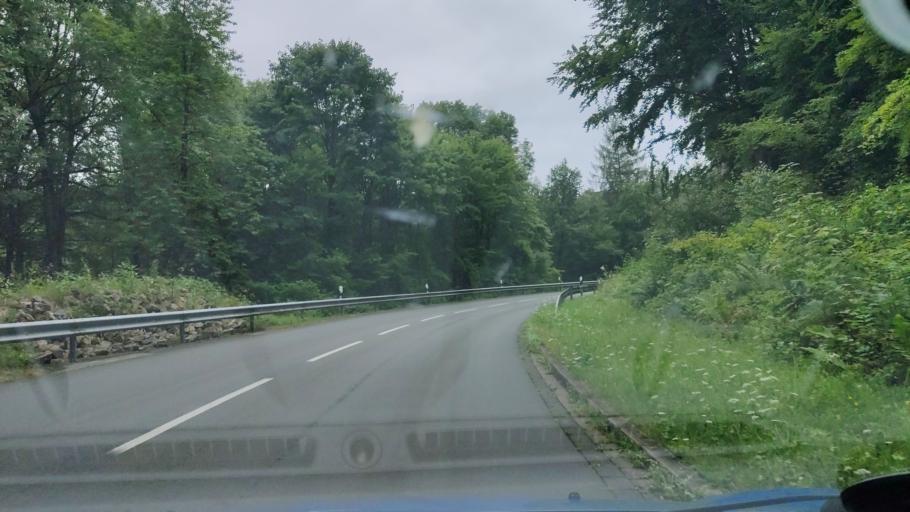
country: DE
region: Lower Saxony
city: Holzminden
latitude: 51.7996
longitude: 9.4817
